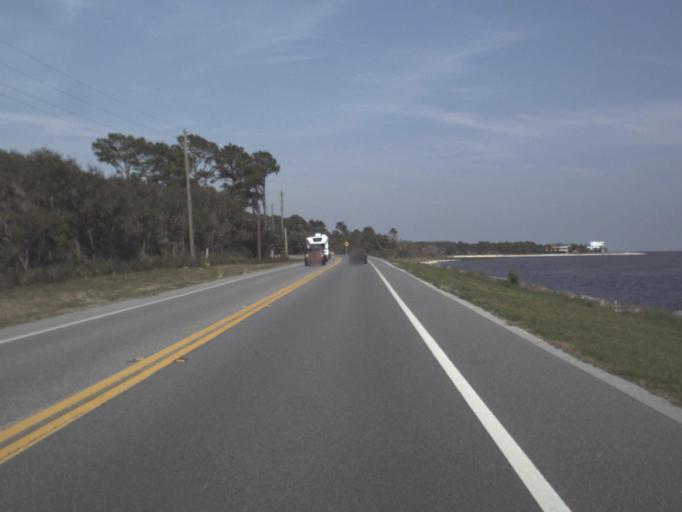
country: US
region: Florida
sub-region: Franklin County
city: Eastpoint
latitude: 29.7844
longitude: -84.7704
